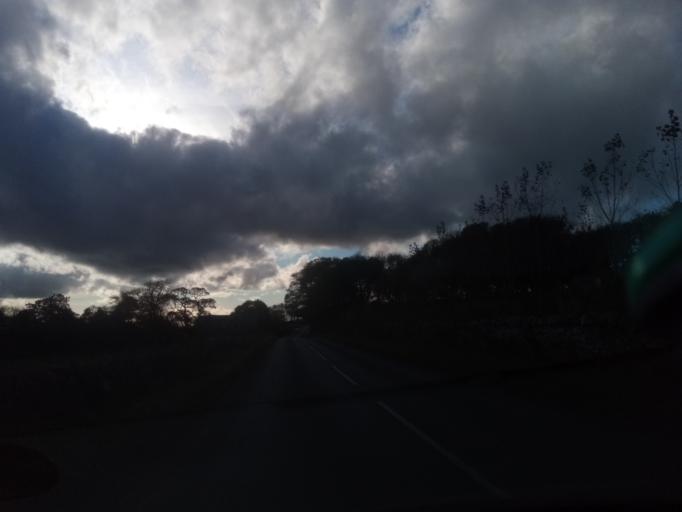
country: GB
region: Scotland
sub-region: The Scottish Borders
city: Chirnside
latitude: 55.8066
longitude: -2.1876
